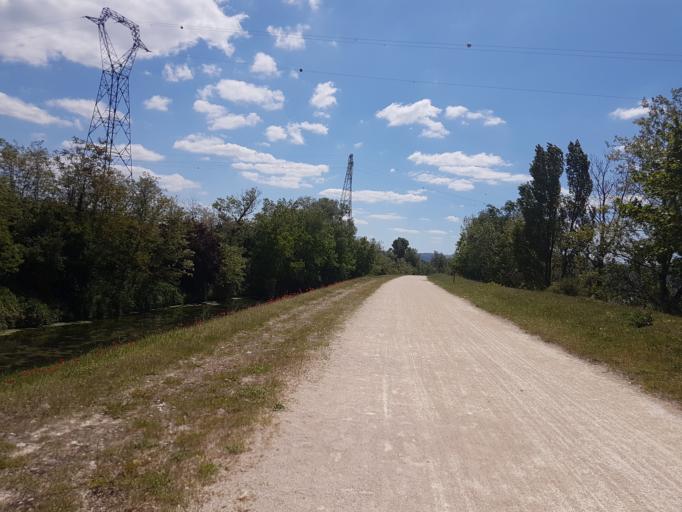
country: FR
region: Rhone-Alpes
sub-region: Departement de l'Ardeche
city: Tournon-sur-Rhone
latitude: 45.0537
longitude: 4.8620
